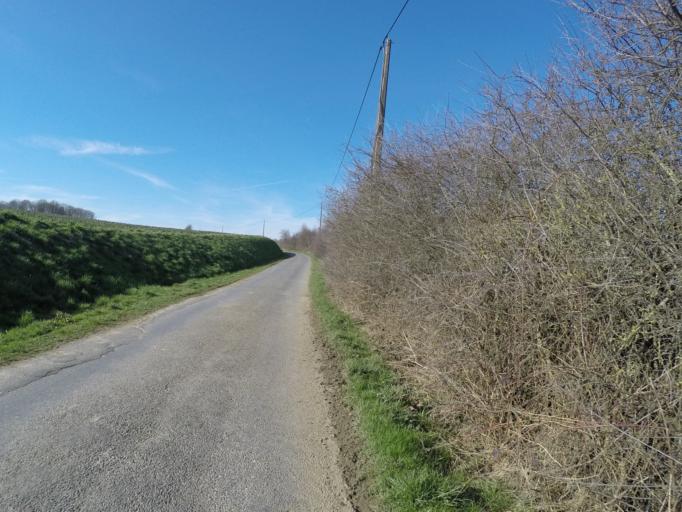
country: BE
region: Wallonia
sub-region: Province de Namur
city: Hamois
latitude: 50.3395
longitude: 5.1422
